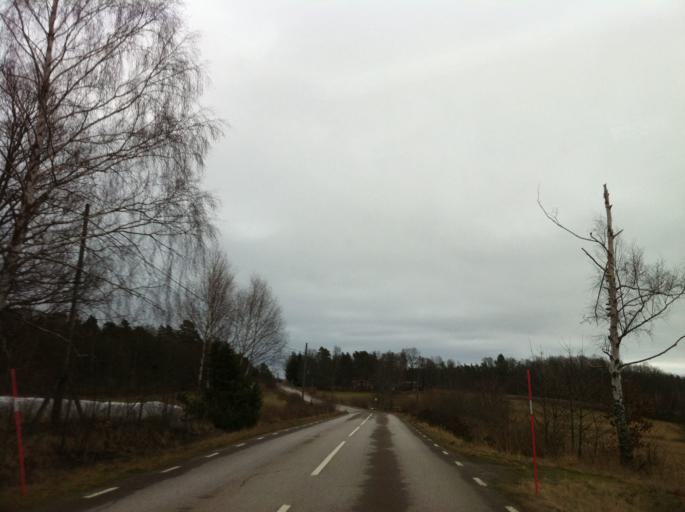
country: SE
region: Kalmar
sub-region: Vasterviks Kommun
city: Vaestervik
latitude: 57.8166
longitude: 16.5785
